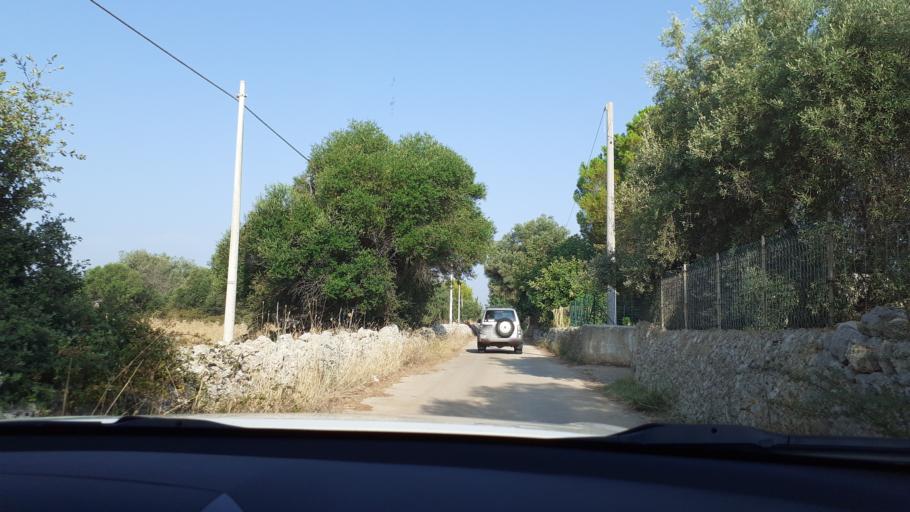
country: IT
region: Sicily
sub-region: Provincia di Siracusa
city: Cassibile
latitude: 36.9804
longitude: 15.1449
